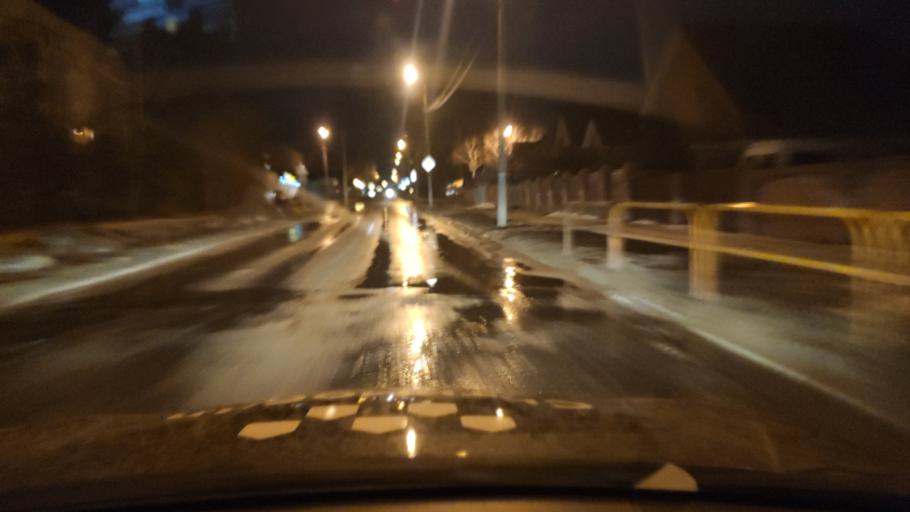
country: RU
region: Samara
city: Povolzhskiy
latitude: 53.5881
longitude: 49.7638
